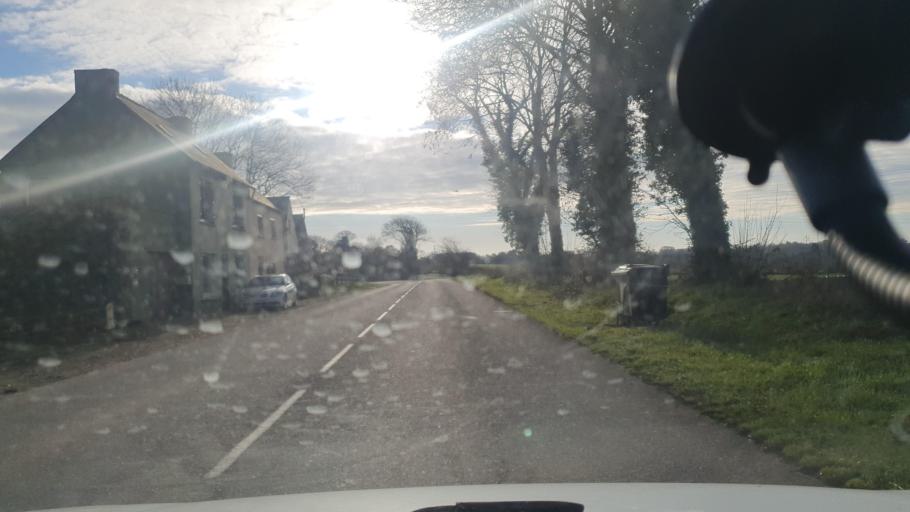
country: FR
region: Brittany
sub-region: Departement du Finistere
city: Briec
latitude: 48.0634
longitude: -4.0204
